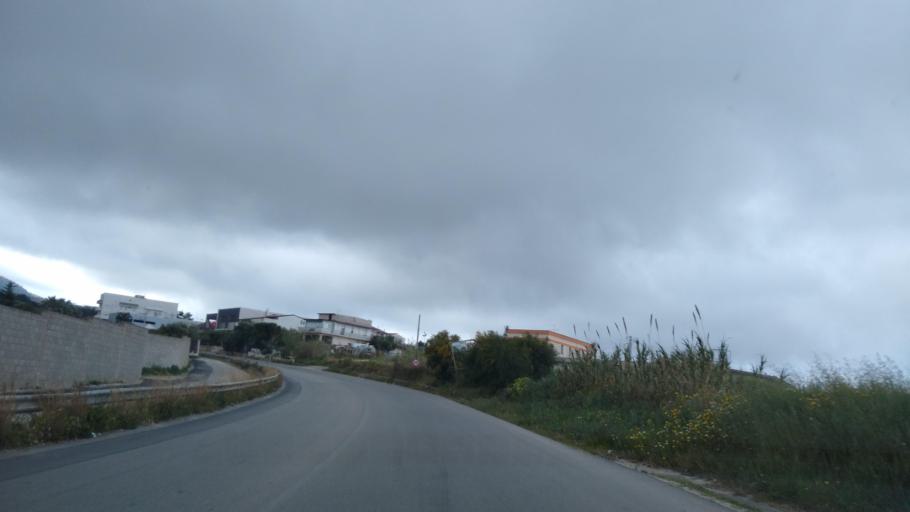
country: IT
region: Sicily
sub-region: Trapani
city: Alcamo
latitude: 37.9906
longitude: 12.9534
